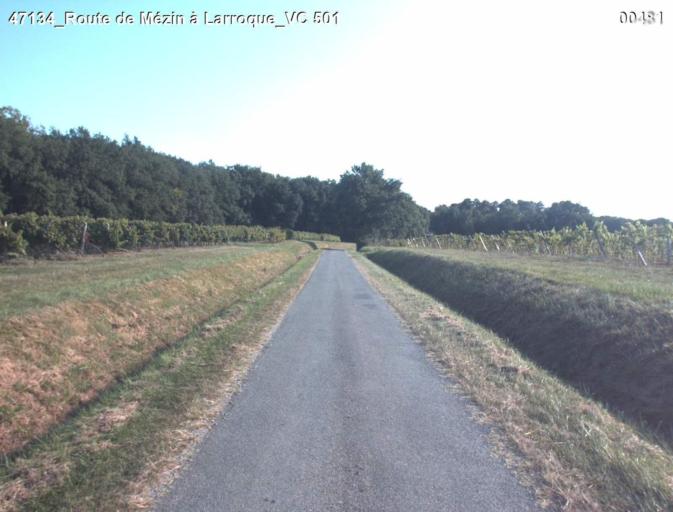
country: FR
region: Aquitaine
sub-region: Departement du Lot-et-Garonne
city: Mezin
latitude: 44.0030
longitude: 0.2784
